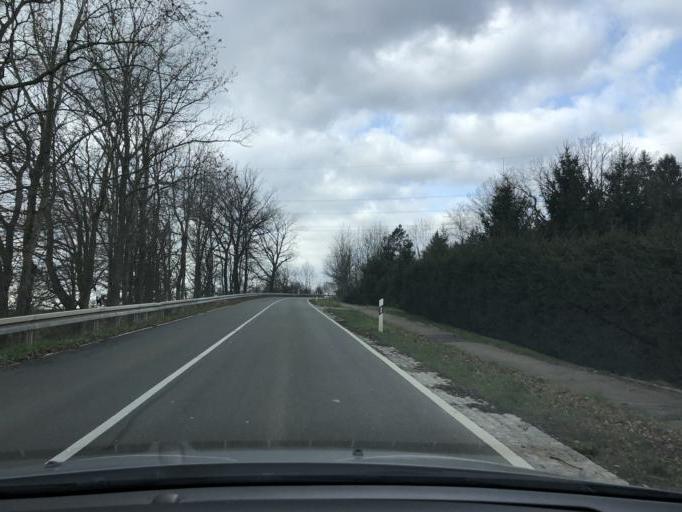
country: DE
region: Saxony
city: Dobeln
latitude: 51.1443
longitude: 13.0912
